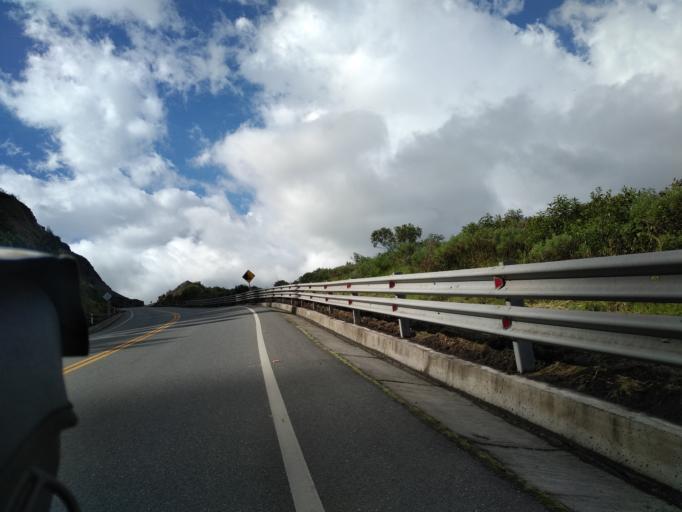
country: EC
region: Tungurahua
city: Banos
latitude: -1.4909
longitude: -78.5174
